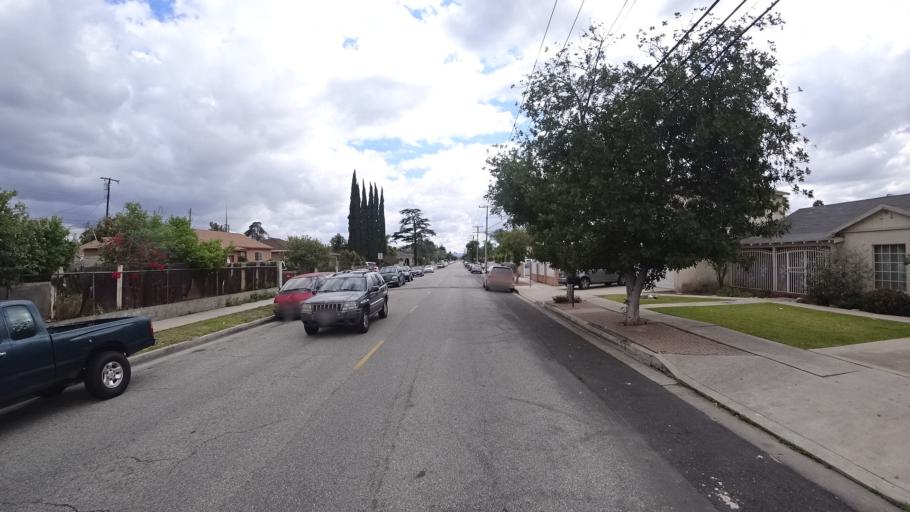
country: US
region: California
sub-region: Los Angeles County
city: Baldwin Park
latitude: 34.0978
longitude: -117.9693
